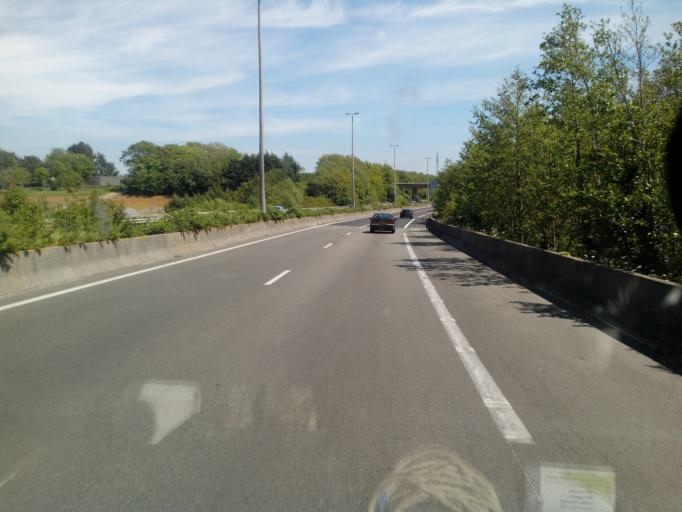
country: FR
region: Nord-Pas-de-Calais
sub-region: Departement du Pas-de-Calais
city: Saint-Martin-Boulogne
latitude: 50.7344
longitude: 1.6423
